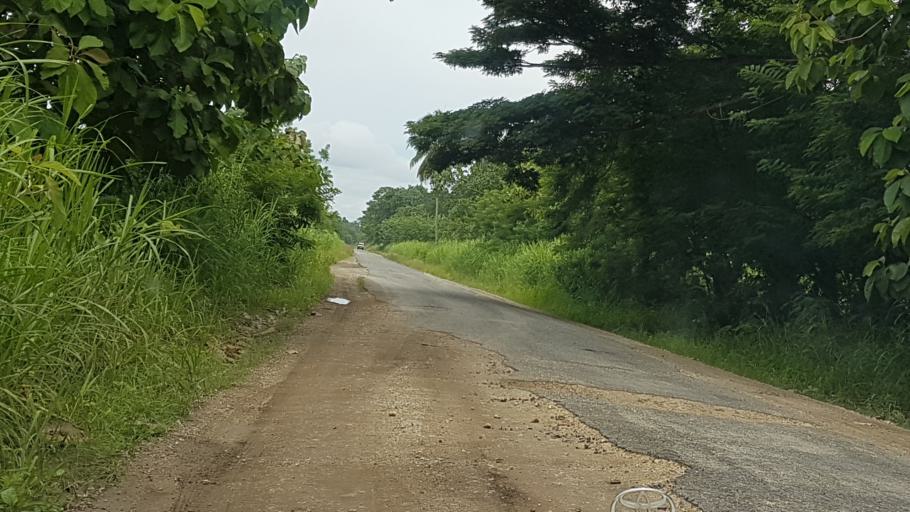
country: PG
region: Madang
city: Madang
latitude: -4.7014
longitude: 145.6189
